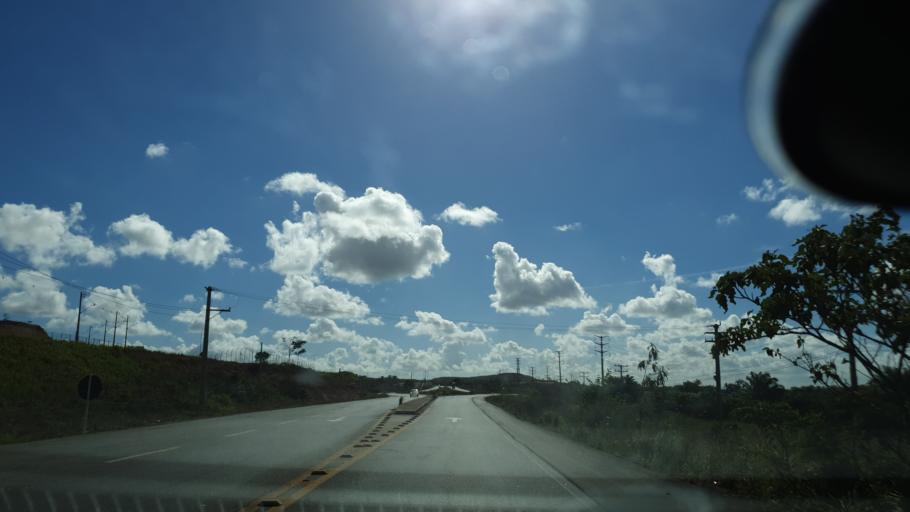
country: BR
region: Bahia
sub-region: Camacari
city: Camacari
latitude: -12.6824
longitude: -38.2451
